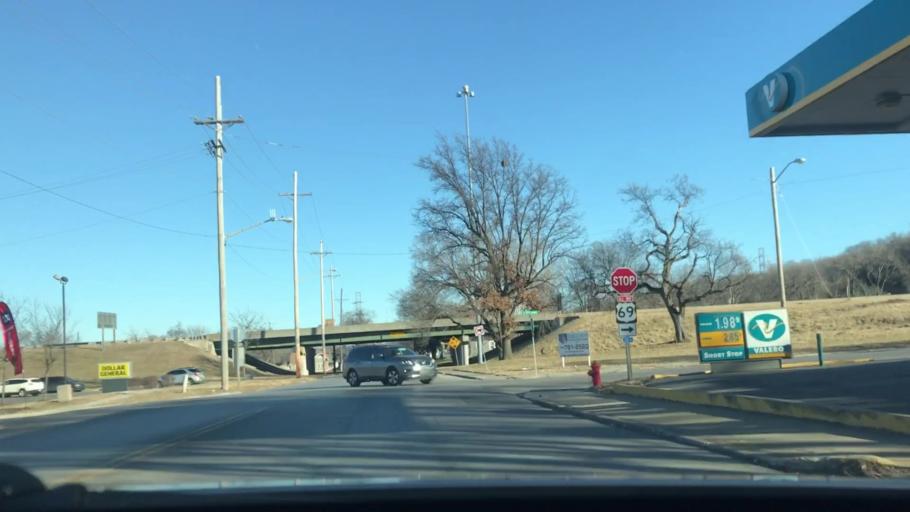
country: US
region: Kansas
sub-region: Johnson County
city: Roeland Park
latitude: 39.0729
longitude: -94.6522
